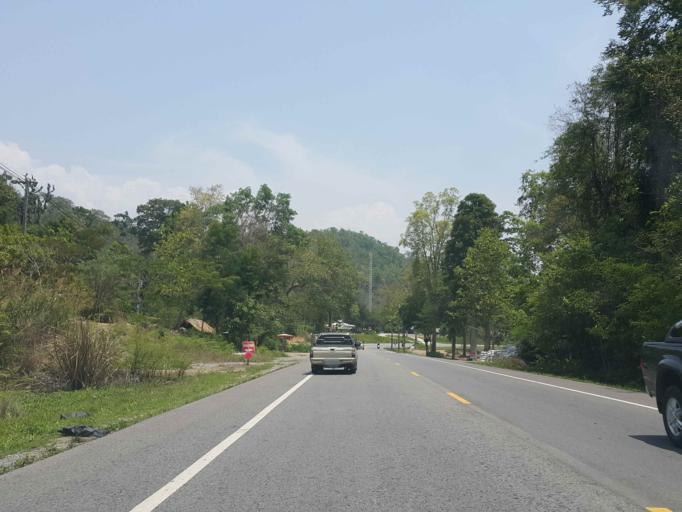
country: TH
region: Chiang Mai
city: Mae On
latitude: 18.9478
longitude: 99.2328
